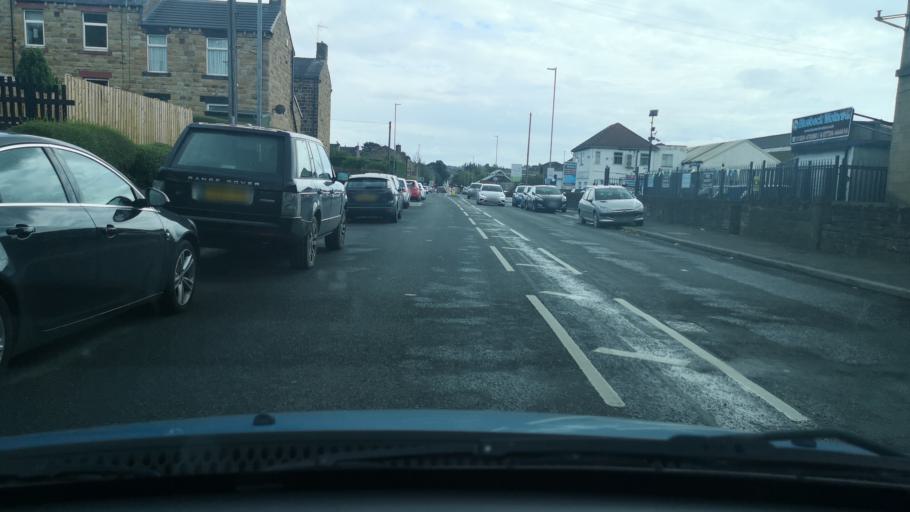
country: GB
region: England
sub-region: Kirklees
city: Batley
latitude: 53.7186
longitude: -1.6395
